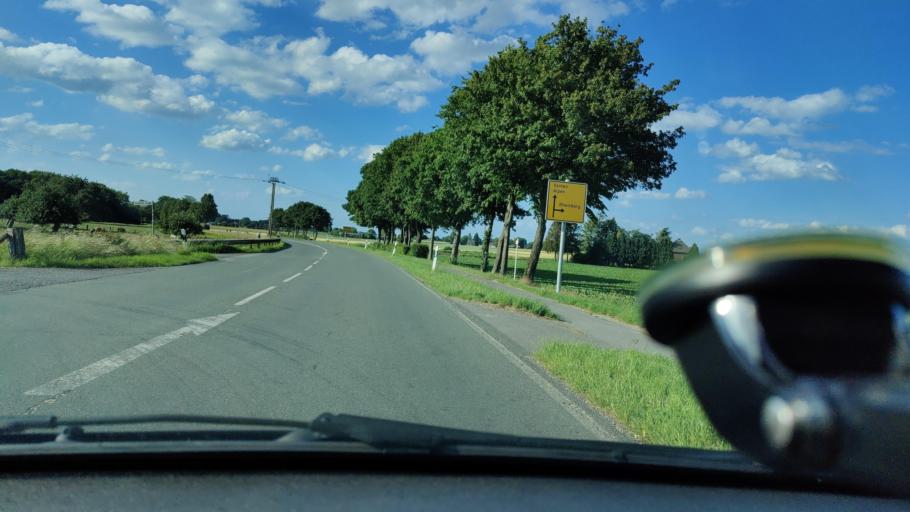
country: DE
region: North Rhine-Westphalia
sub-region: Regierungsbezirk Dusseldorf
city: Kamp-Lintfort
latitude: 51.5413
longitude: 6.5339
